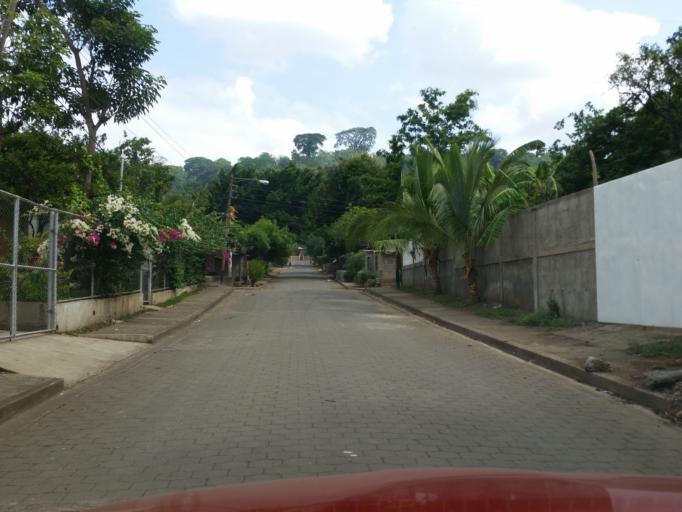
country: NI
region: Masaya
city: La Concepcion
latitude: 11.9523
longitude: -86.1865
